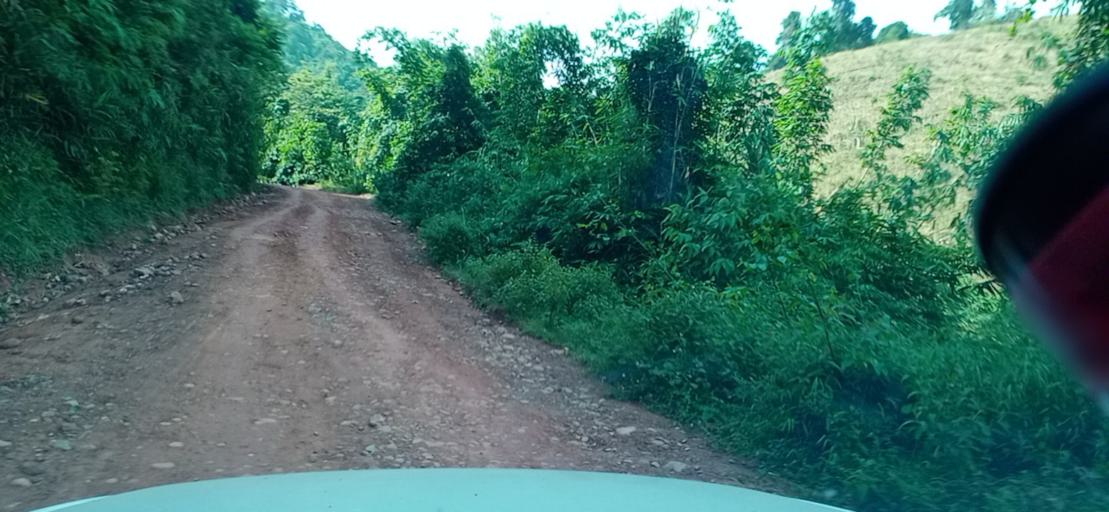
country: TH
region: Changwat Bueng Kan
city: Pak Khat
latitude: 18.6657
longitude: 103.1982
